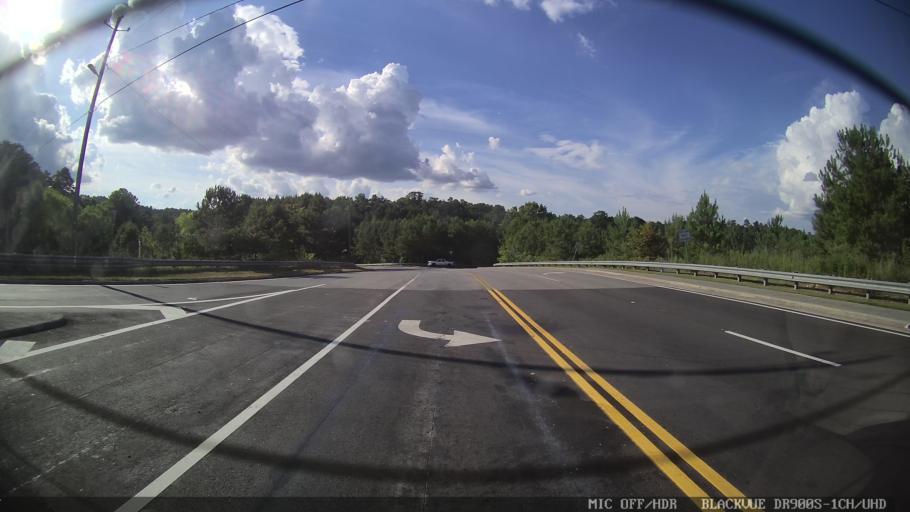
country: US
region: Georgia
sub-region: Floyd County
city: Rome
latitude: 34.2199
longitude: -85.1326
